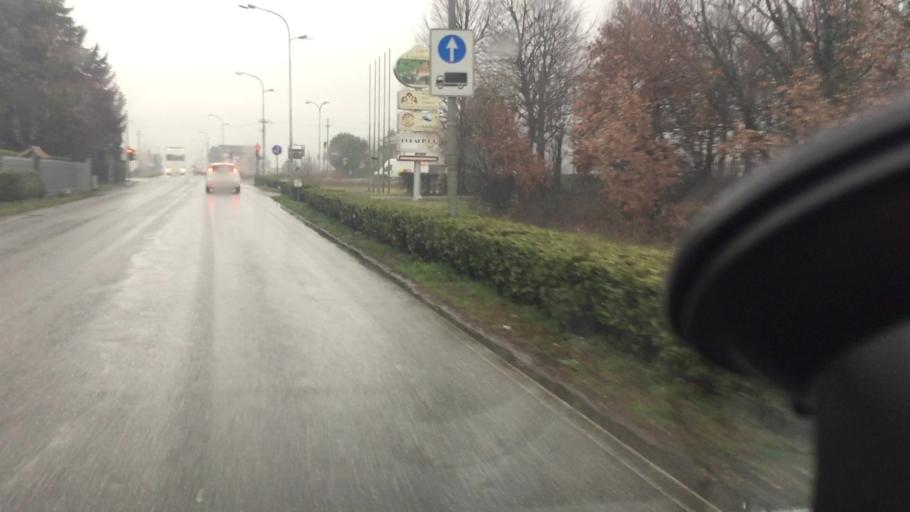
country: IT
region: Lombardy
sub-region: Citta metropolitana di Milano
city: Vaprio d'Adda
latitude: 45.5849
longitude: 9.5216
